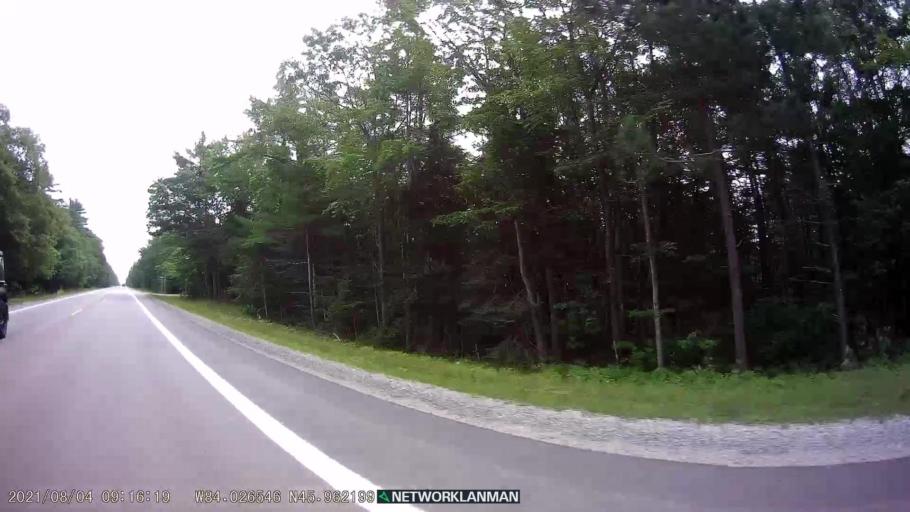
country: CA
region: Ontario
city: Thessalon
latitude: 45.9622
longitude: -84.0260
